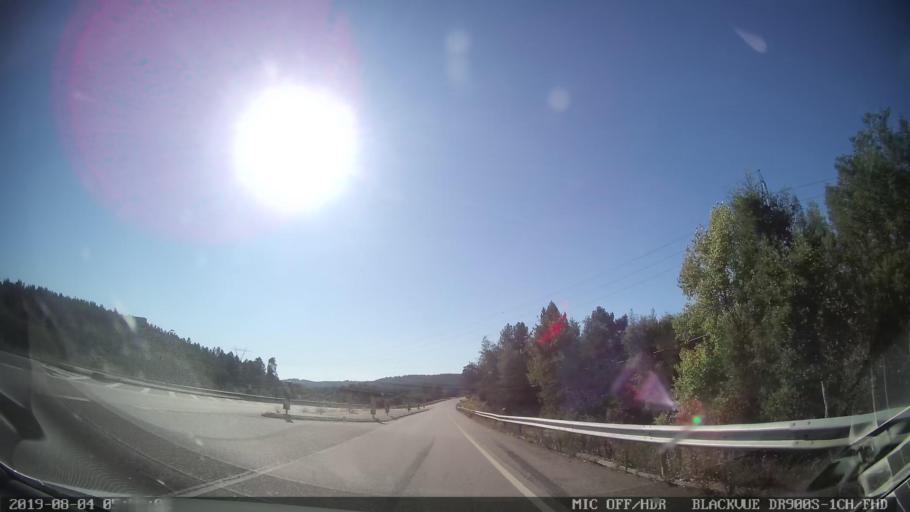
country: PT
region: Portalegre
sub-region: Gaviao
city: Gaviao
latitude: 39.4507
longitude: -7.9225
